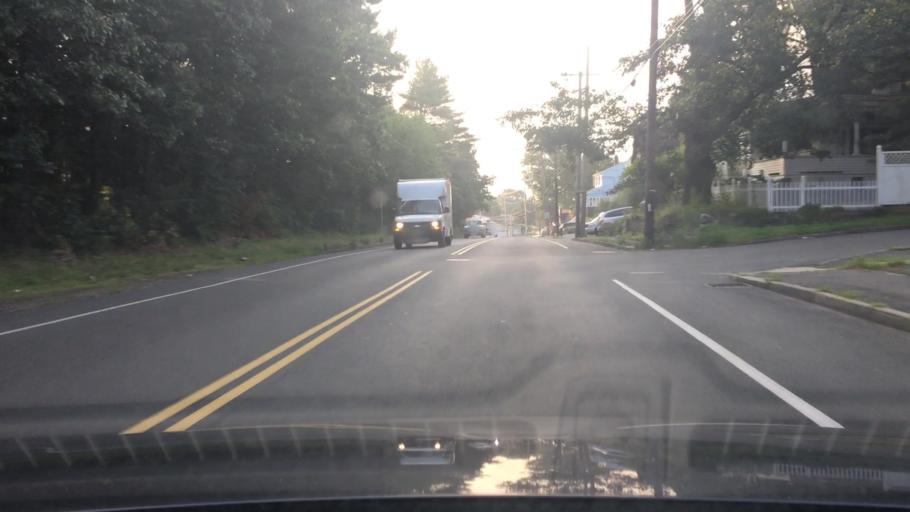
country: US
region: Massachusetts
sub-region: Essex County
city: Saugus
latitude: 42.4750
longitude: -70.9959
